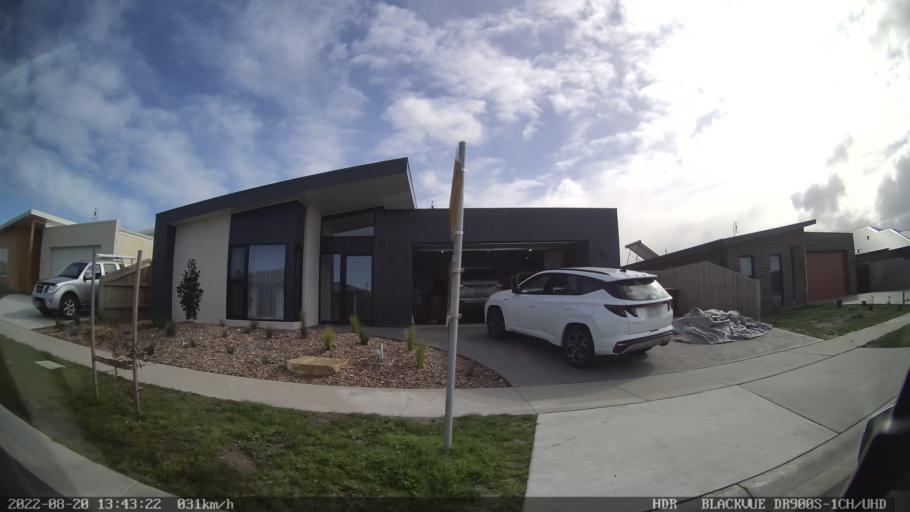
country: AU
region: Victoria
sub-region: Bass Coast
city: North Wonthaggi
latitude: -38.6029
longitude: 145.6126
